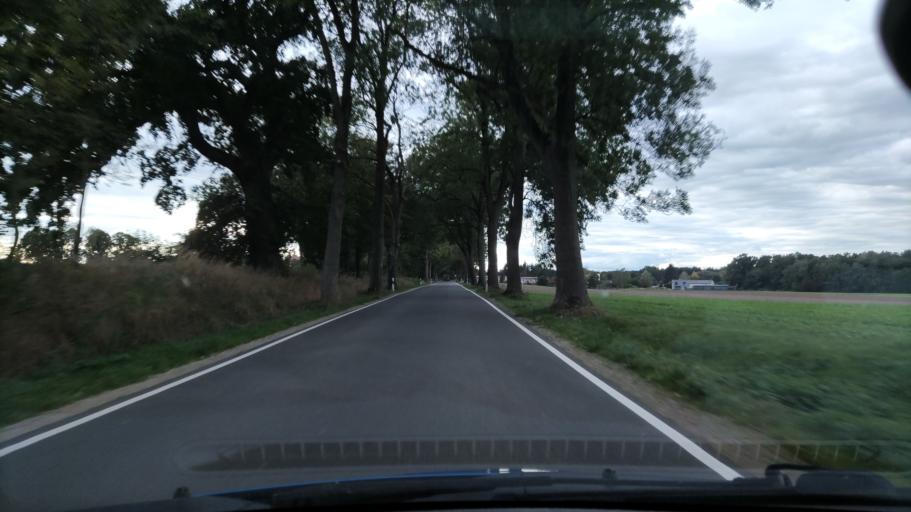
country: DE
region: Mecklenburg-Vorpommern
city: Zarrentin
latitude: 53.4620
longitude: 10.9782
